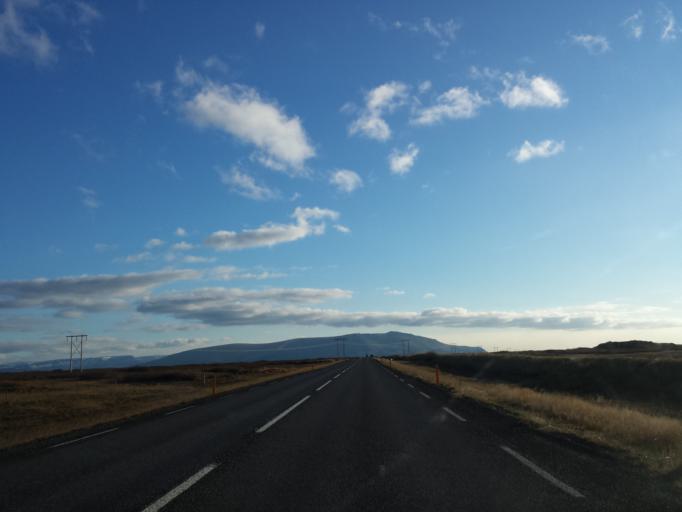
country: IS
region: West
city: Borgarnes
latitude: 64.4584
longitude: -21.9615
